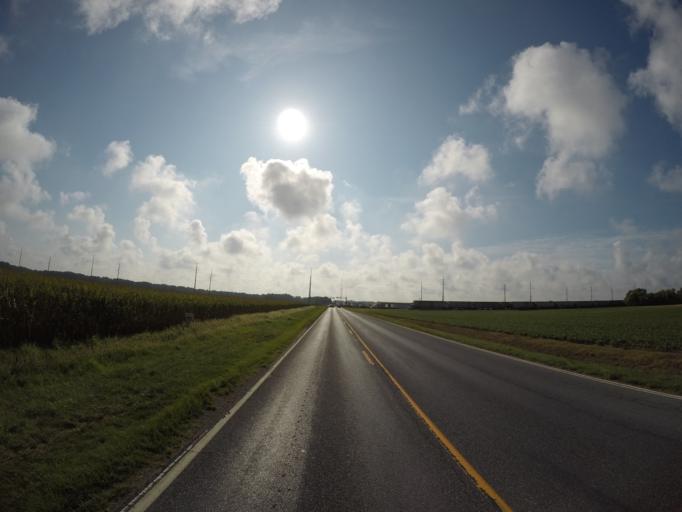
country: US
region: Delaware
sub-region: Sussex County
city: Bridgeville
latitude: 38.7616
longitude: -75.6044
